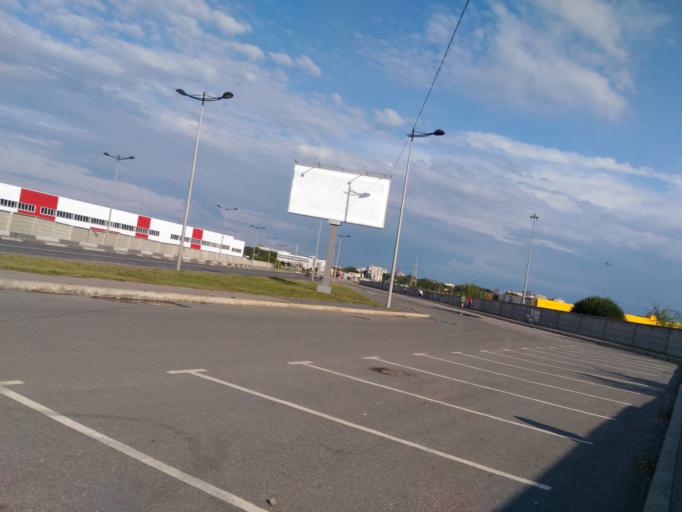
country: RU
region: Ulyanovsk
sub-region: Ulyanovskiy Rayon
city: Ulyanovsk
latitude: 54.2894
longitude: 48.2730
